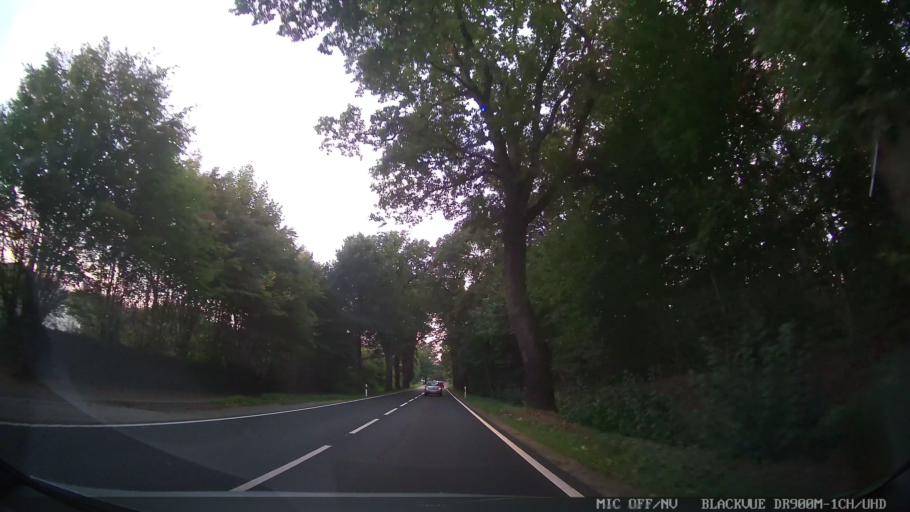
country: DE
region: Schleswig-Holstein
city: Ratekau
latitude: 53.9442
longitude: 10.7225
